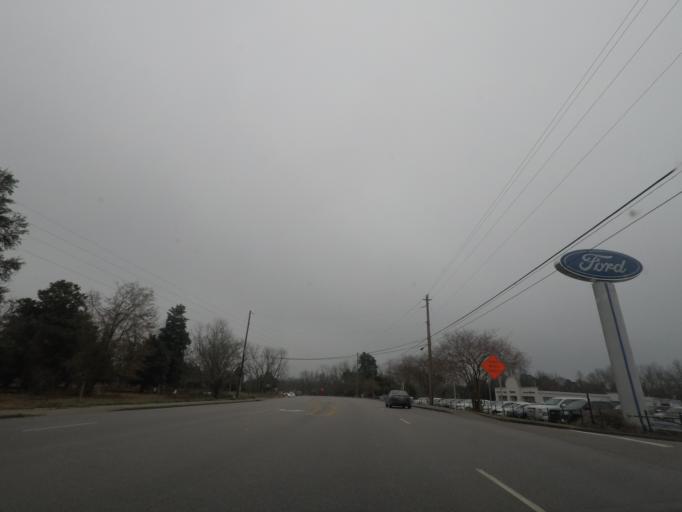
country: US
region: South Carolina
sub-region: Clarendon County
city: Manning
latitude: 33.7003
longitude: -80.2372
